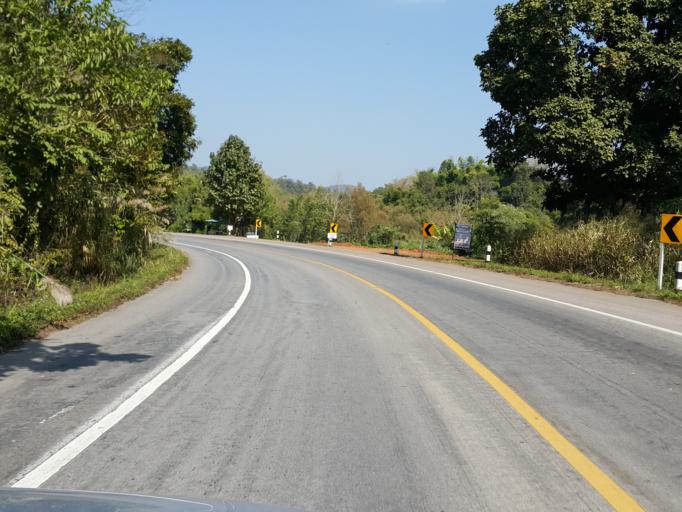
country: TH
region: Lampang
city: Wang Nuea
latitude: 19.1013
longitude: 99.4496
